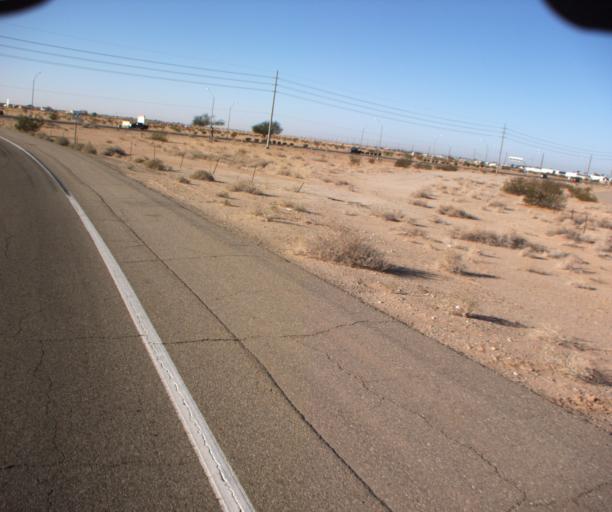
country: US
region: Arizona
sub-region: Yuma County
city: Fortuna Foothills
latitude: 32.6716
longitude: -114.4955
